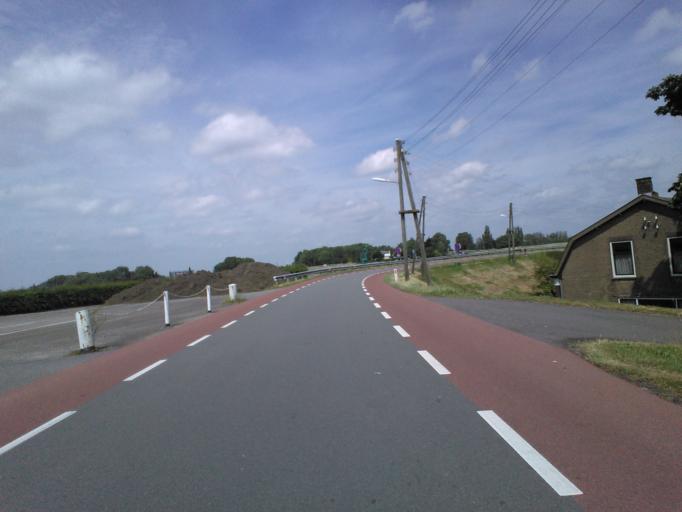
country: NL
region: South Holland
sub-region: Gemeente Gouda
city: Bloemendaal
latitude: 51.9747
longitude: 4.6543
